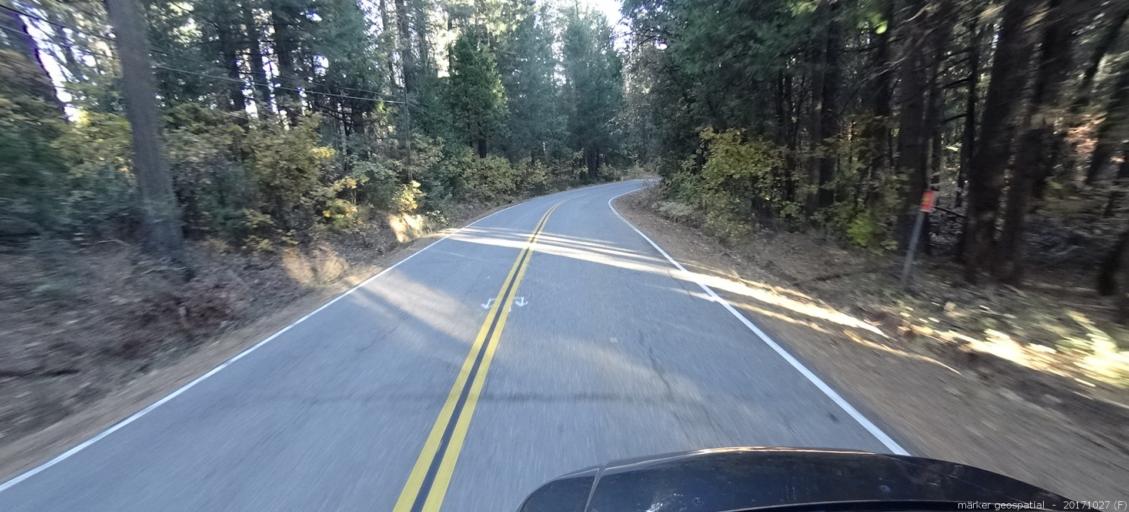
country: US
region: California
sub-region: Shasta County
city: Burney
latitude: 40.9994
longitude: -121.9174
